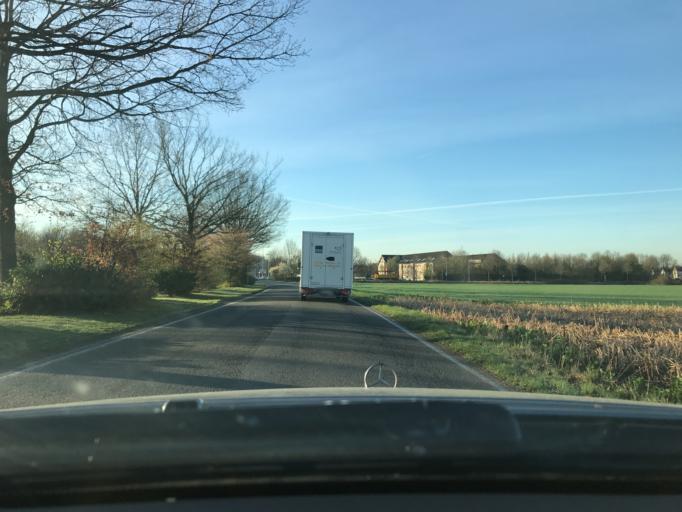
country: DE
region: North Rhine-Westphalia
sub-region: Regierungsbezirk Dusseldorf
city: Krefeld
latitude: 51.3749
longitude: 6.6136
